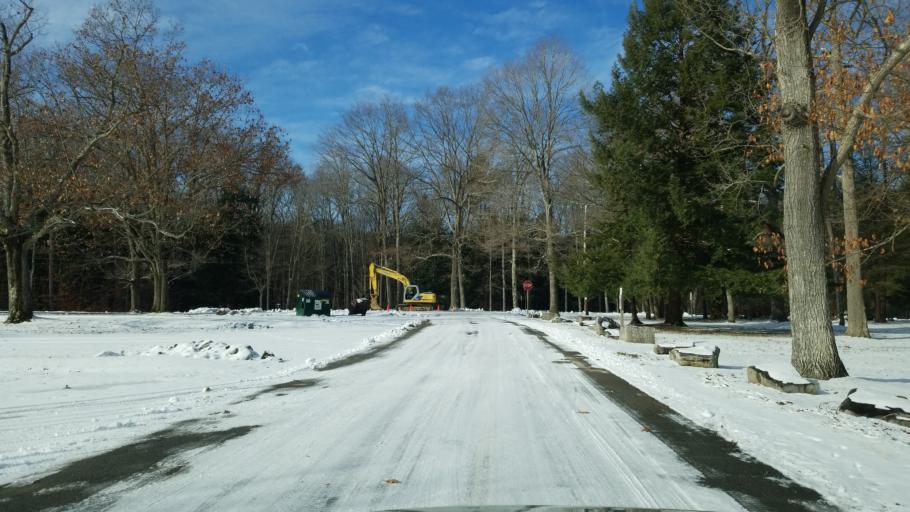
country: US
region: Pennsylvania
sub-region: Clearfield County
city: Clearfield
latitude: 41.1946
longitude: -78.5103
